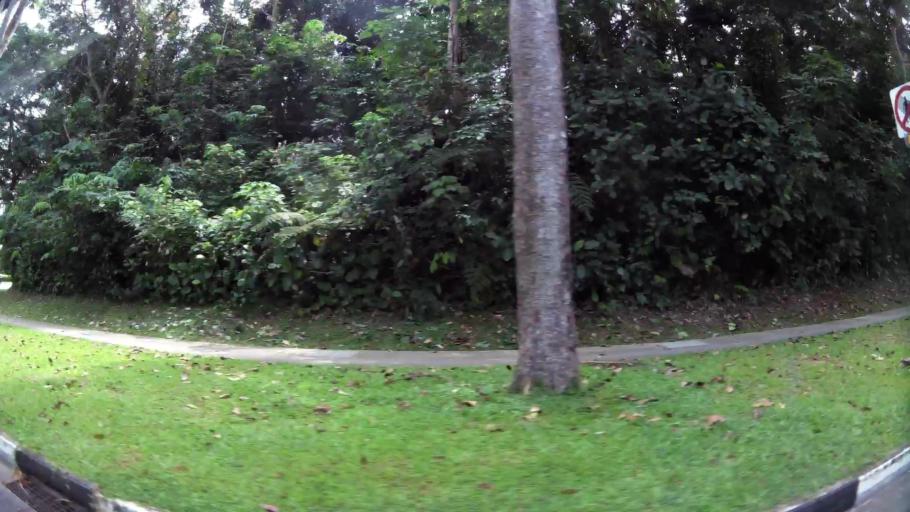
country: SG
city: Singapore
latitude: 1.3486
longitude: 103.7697
